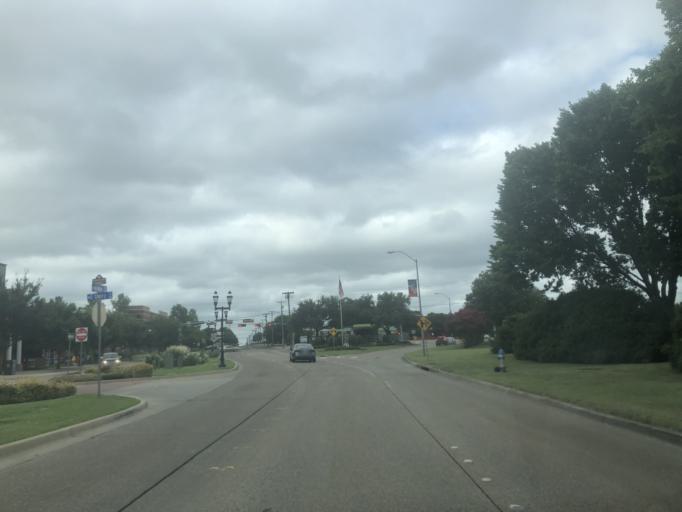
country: US
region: Texas
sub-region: Dallas County
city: Duncanville
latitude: 32.6529
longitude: -96.9084
